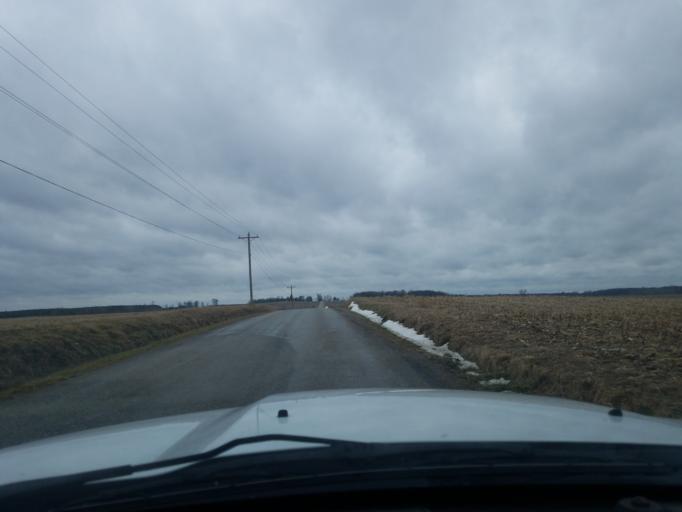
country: US
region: Indiana
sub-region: Noble County
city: Albion
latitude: 41.4337
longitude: -85.3949
